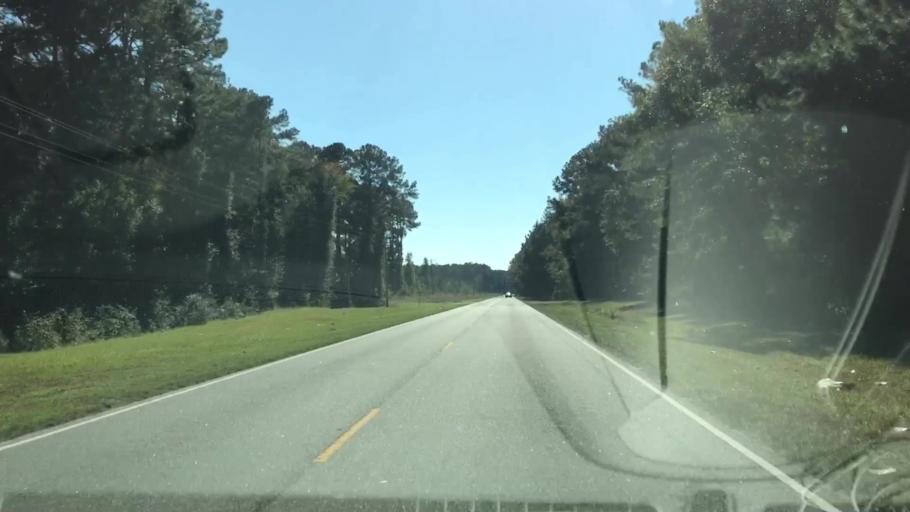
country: US
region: South Carolina
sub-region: Jasper County
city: Ridgeland
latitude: 32.4465
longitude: -80.8968
